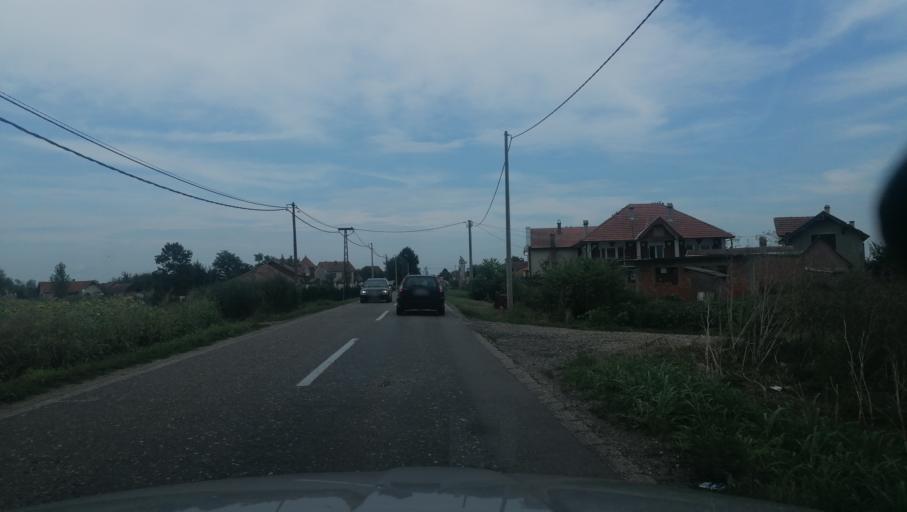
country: RS
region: Central Serbia
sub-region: Macvanski Okrug
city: Bogatic
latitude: 44.8270
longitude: 19.4607
